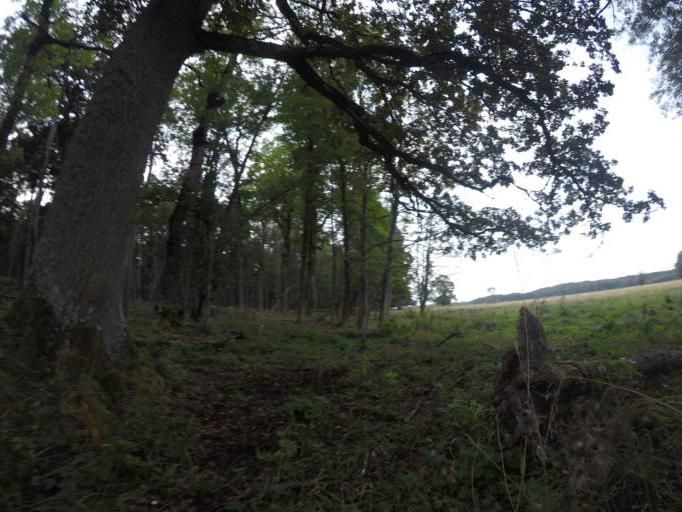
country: SE
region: Vaestmanland
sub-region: Hallstahammars Kommun
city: Kolback
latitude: 59.4693
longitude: 16.2199
